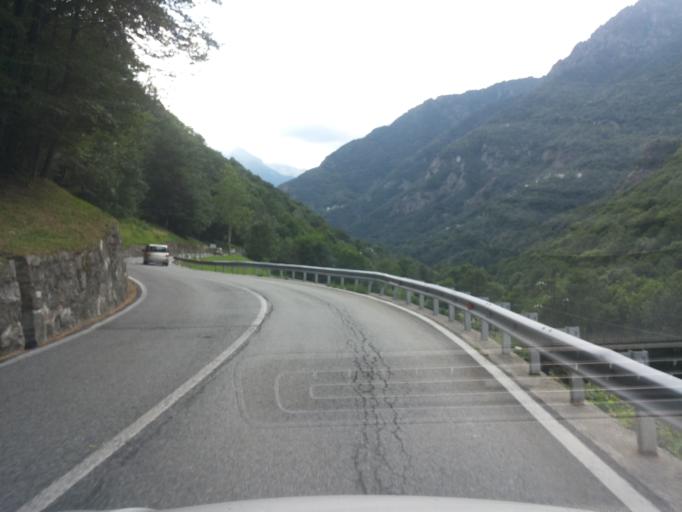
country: IT
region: Aosta Valley
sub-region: Valle d'Aosta
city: Lillianes
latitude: 45.6257
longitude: 7.8327
